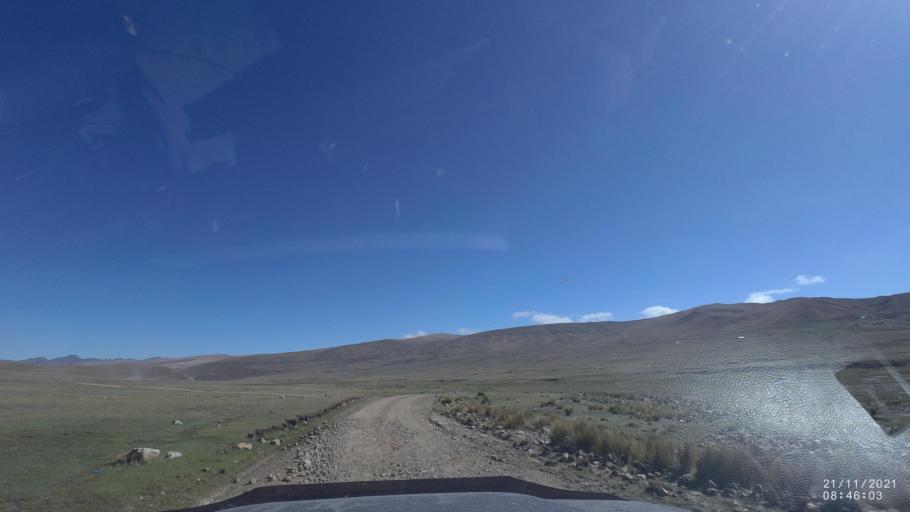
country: BO
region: Cochabamba
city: Cochabamba
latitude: -17.2451
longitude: -66.2320
